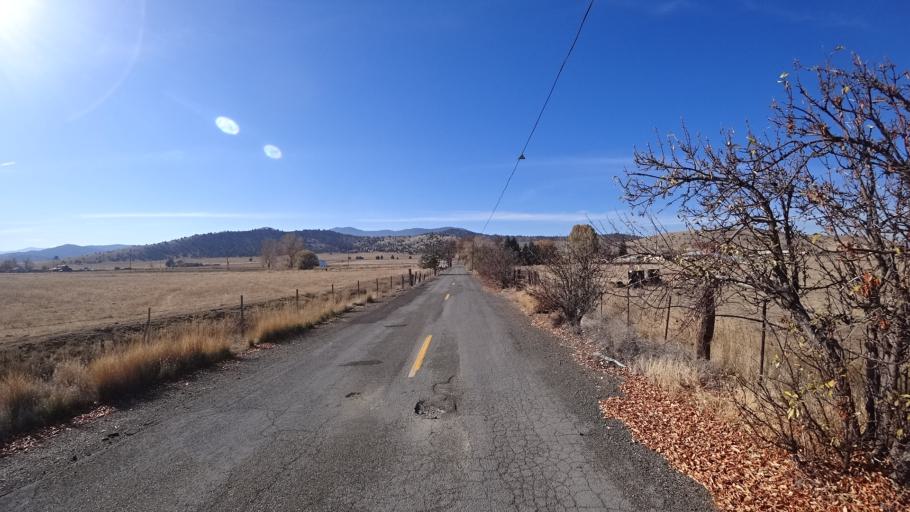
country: US
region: California
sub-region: Siskiyou County
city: Montague
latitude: 41.6326
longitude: -122.5276
